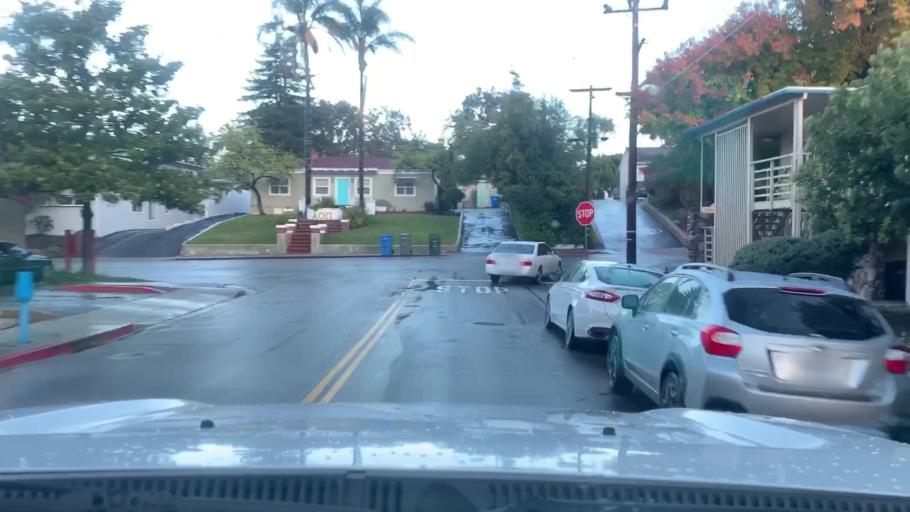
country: US
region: California
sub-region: San Luis Obispo County
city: San Luis Obispo
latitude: 35.2955
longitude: -120.6622
